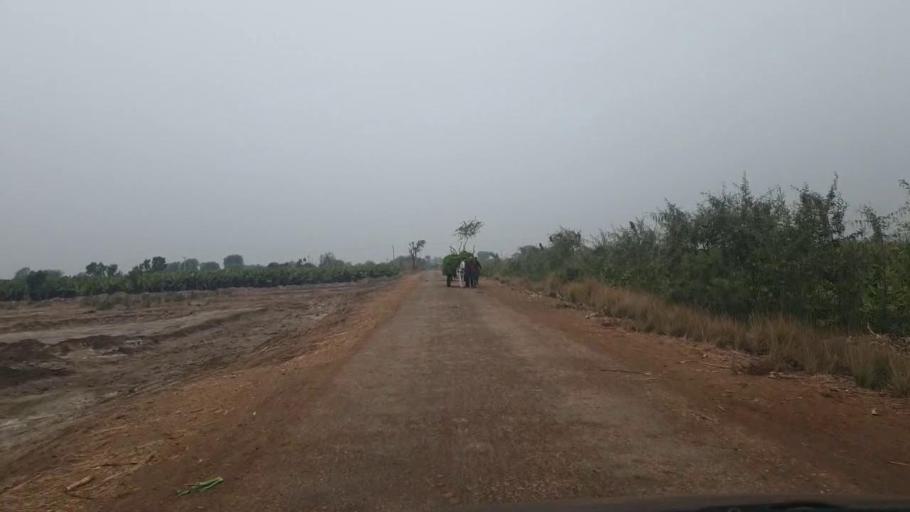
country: PK
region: Sindh
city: Tando Adam
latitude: 25.8310
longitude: 68.6799
